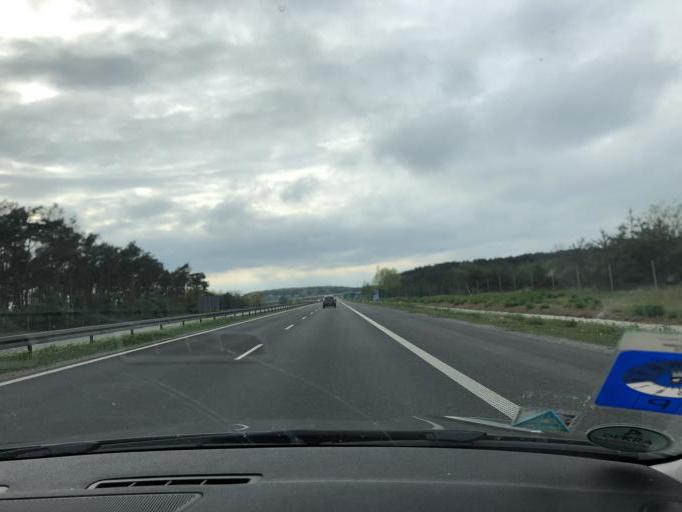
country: PL
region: Opole Voivodeship
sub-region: Powiat krapkowicki
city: Gogolin
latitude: 50.4843
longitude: 18.0054
